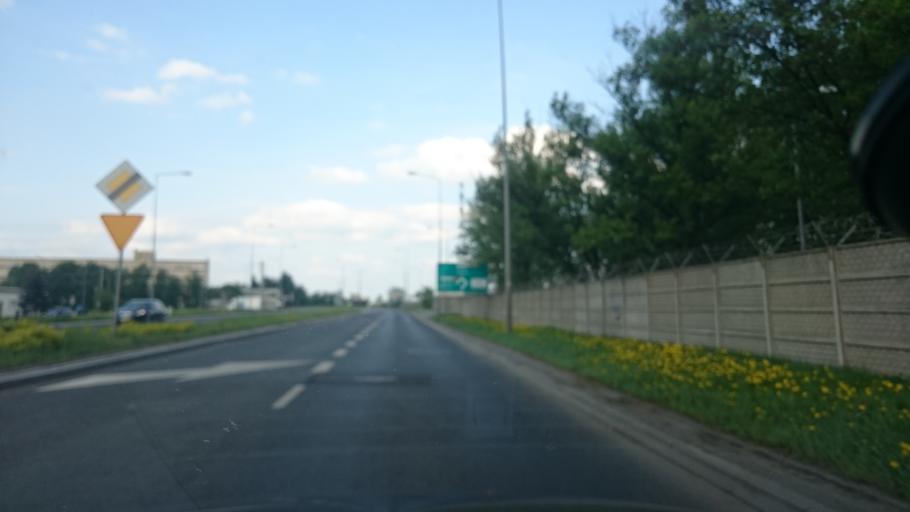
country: PL
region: Kujawsko-Pomorskie
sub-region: Grudziadz
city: Grudziadz
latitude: 53.4758
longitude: 18.7770
